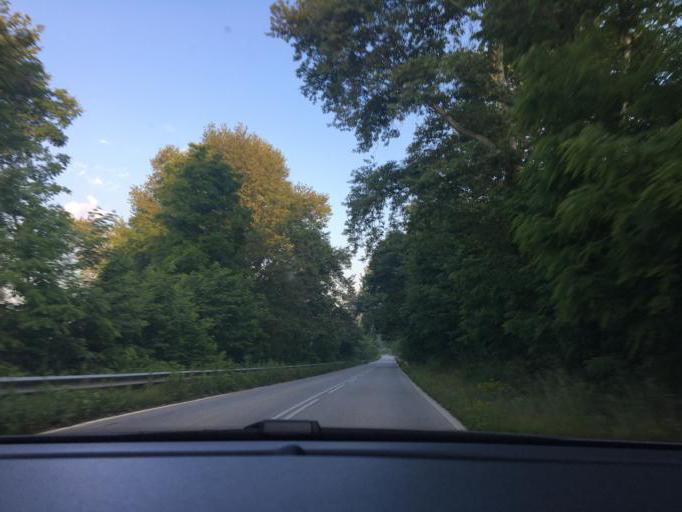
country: MK
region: Novo Selo
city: Novo Selo
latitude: 41.3970
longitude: 22.9986
